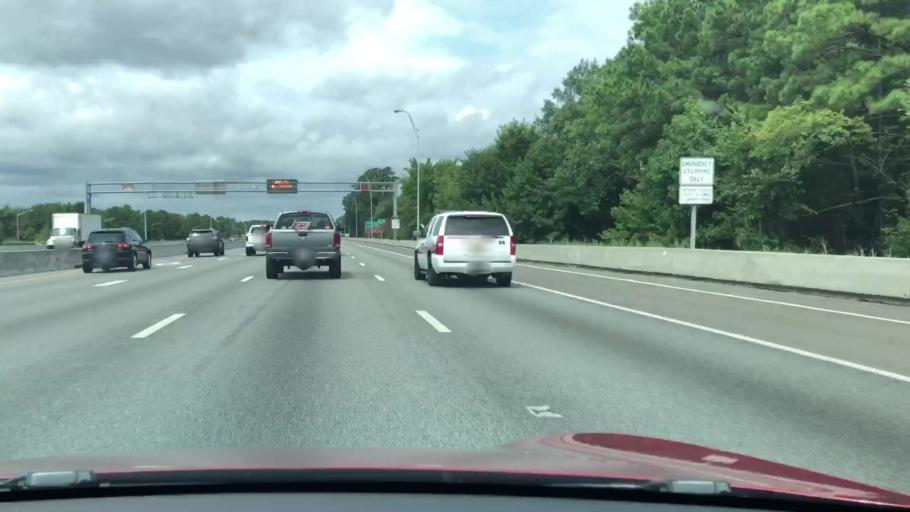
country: US
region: Virginia
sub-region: City of Virginia Beach
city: Virginia Beach
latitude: 36.8316
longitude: -76.1212
